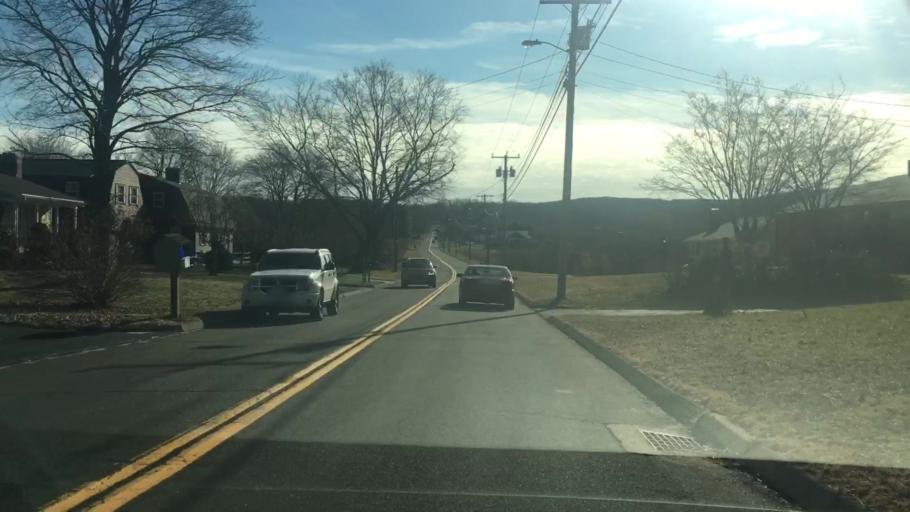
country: US
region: Connecticut
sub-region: Middlesex County
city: Middletown
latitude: 41.5286
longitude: -72.6503
